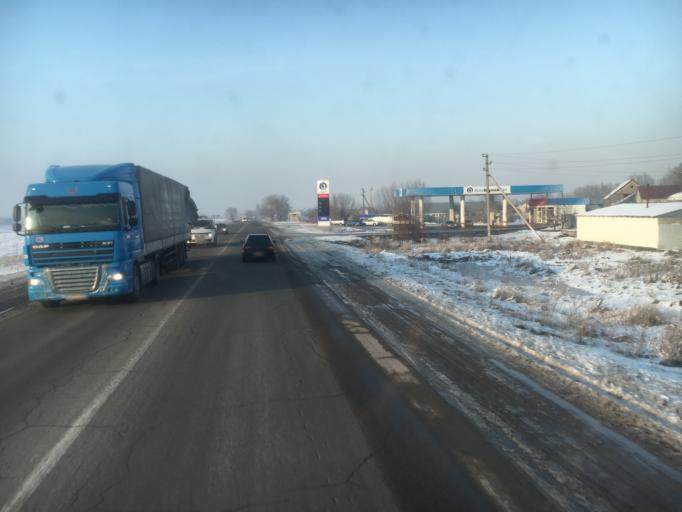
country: KZ
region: Almaty Oblysy
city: Burunday
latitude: 43.2892
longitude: 76.6734
